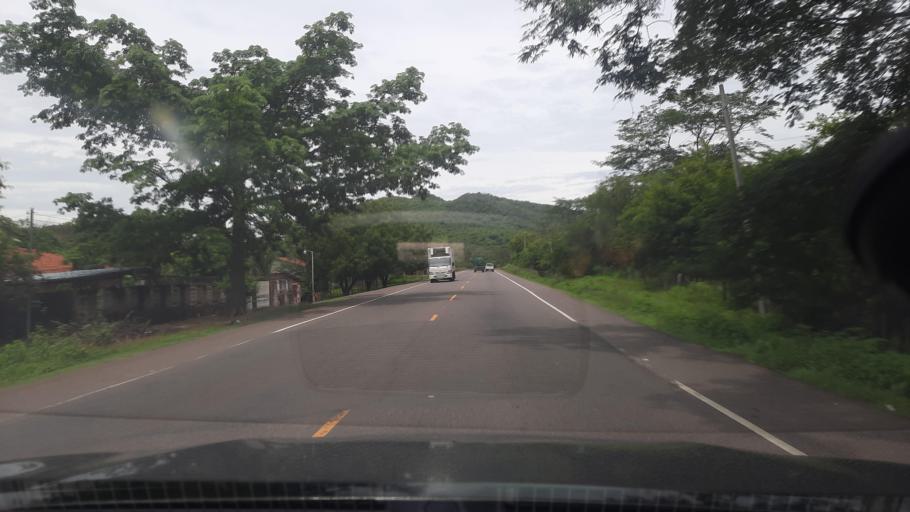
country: HN
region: Valle
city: Langue
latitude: 13.5946
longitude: -87.7025
